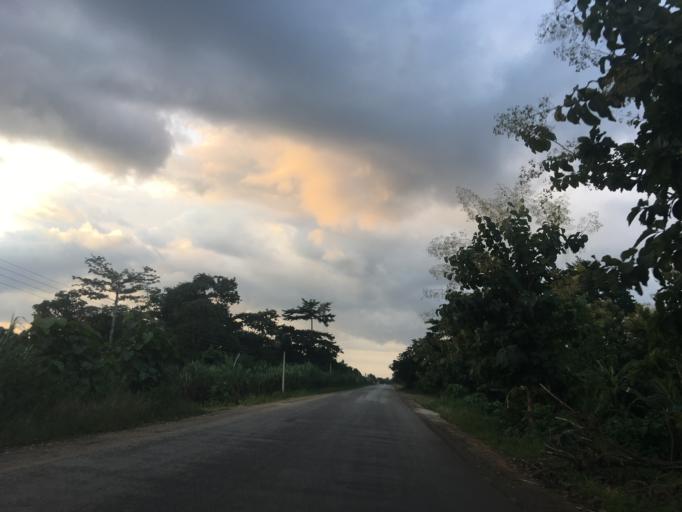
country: GH
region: Western
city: Bibiani
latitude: 6.7513
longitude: -2.5045
